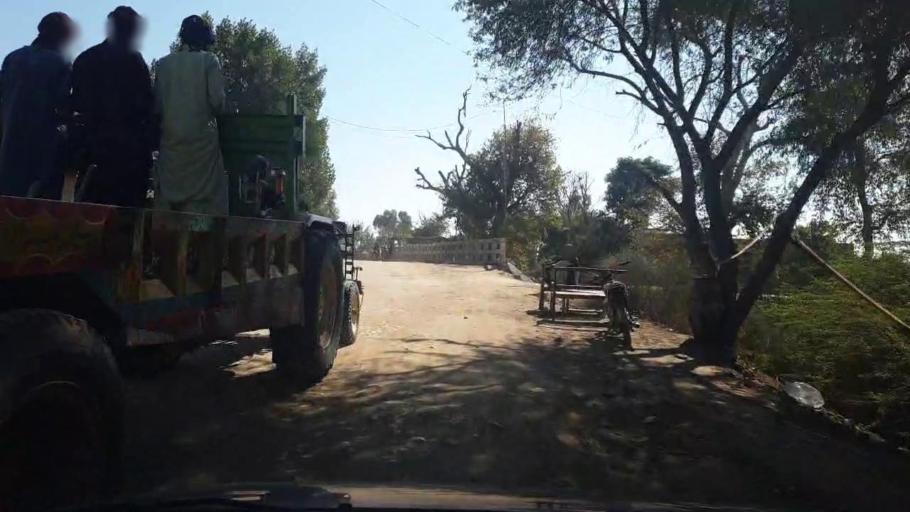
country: PK
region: Sindh
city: Bozdar
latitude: 27.0702
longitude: 68.6194
